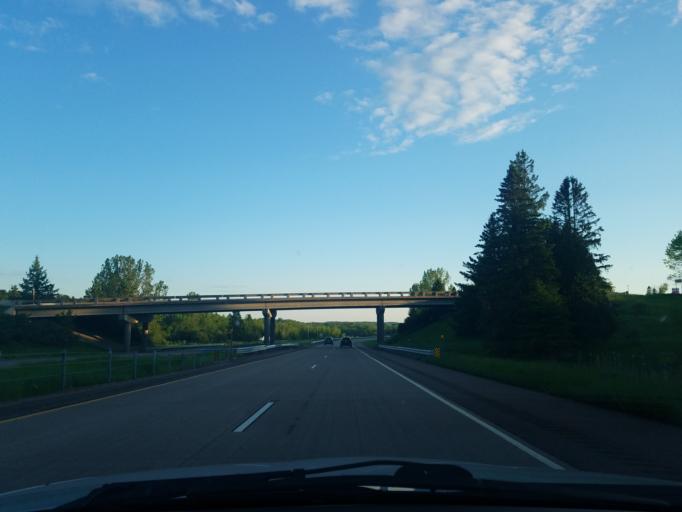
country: US
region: Minnesota
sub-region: Carlton County
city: Moose Lake
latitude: 46.5061
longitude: -92.6743
